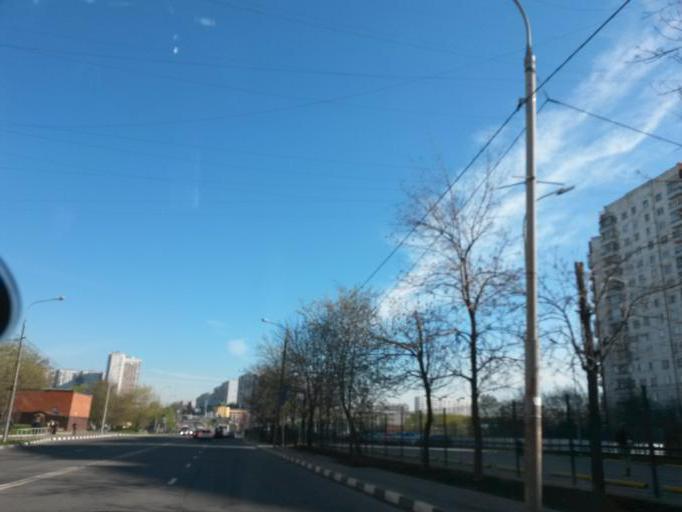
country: RU
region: Moskovskaya
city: Razvilka
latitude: 55.6088
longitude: 37.7446
